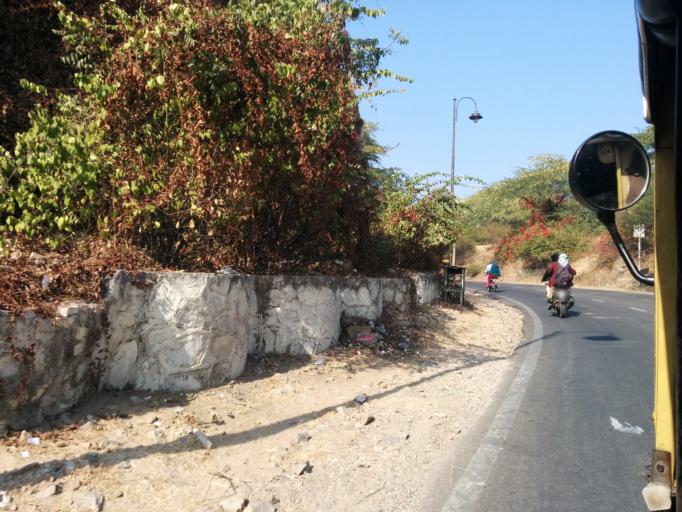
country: IN
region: Rajasthan
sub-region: Jaipur
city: Jaipur
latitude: 26.9646
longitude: 75.8467
